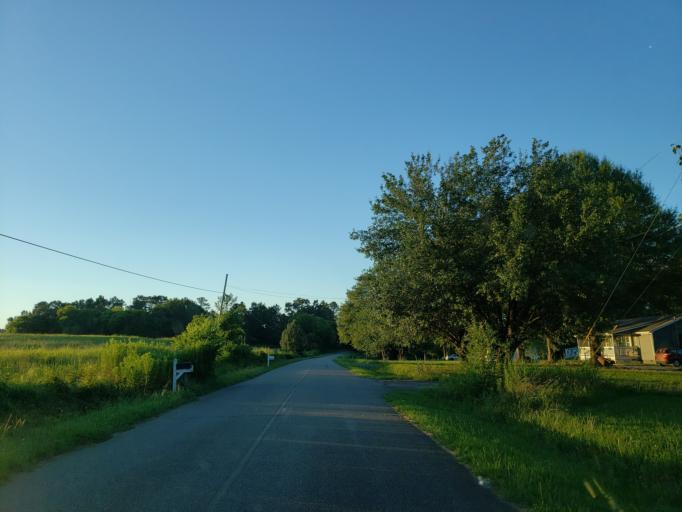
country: US
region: Georgia
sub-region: Bartow County
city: Euharlee
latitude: 34.0834
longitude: -84.9100
